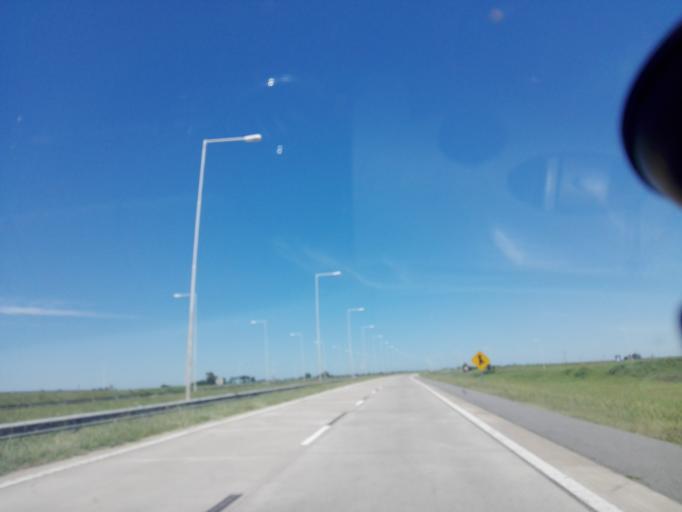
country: AR
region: Santa Fe
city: Carcarana
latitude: -32.8682
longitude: -61.2534
